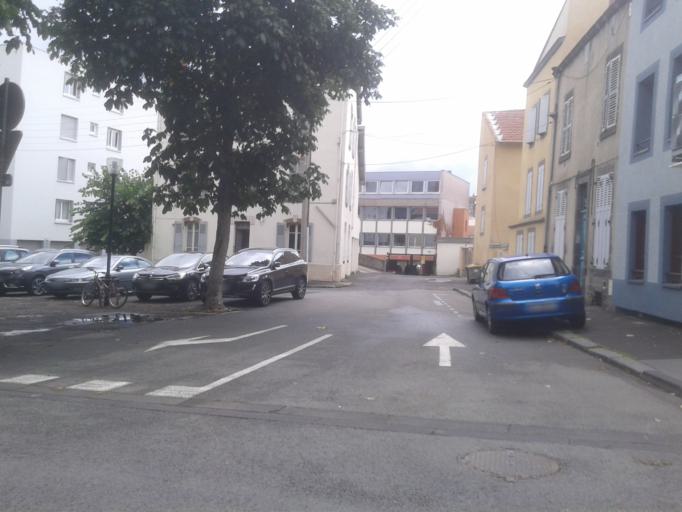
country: FR
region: Auvergne
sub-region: Departement du Puy-de-Dome
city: Clermont-Ferrand
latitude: 45.7854
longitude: 3.0862
